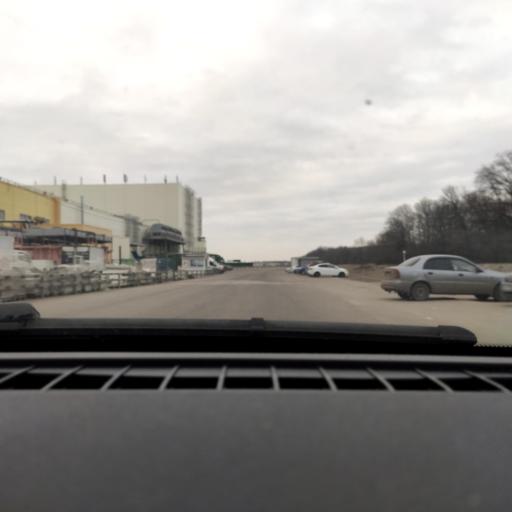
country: RU
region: Voronezj
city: Podgornoye
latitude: 51.7867
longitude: 39.2054
